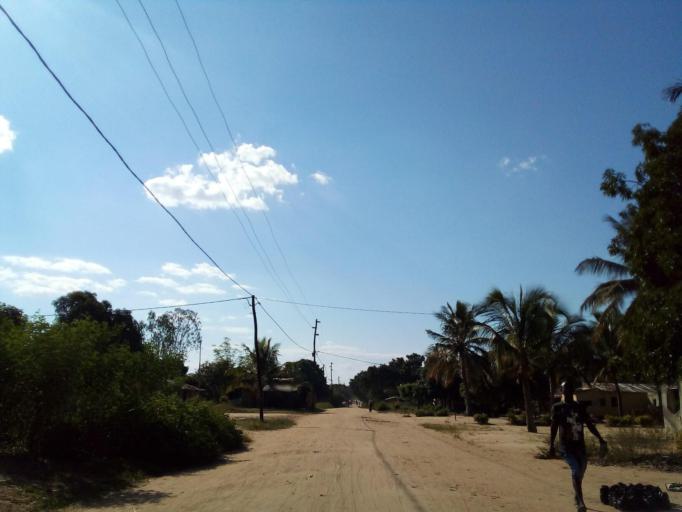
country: MZ
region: Zambezia
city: Quelimane
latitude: -17.5627
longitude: 36.6993
